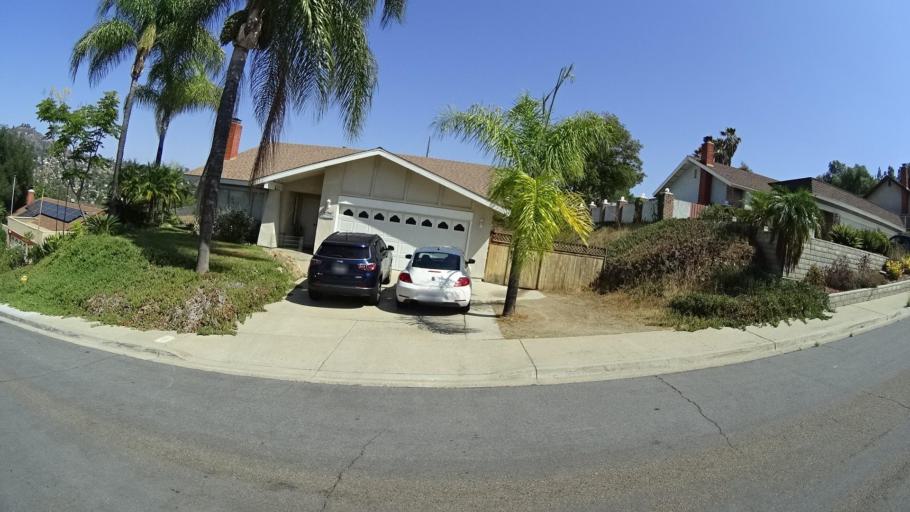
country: US
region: California
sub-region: San Diego County
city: Spring Valley
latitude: 32.7434
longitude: -116.9855
